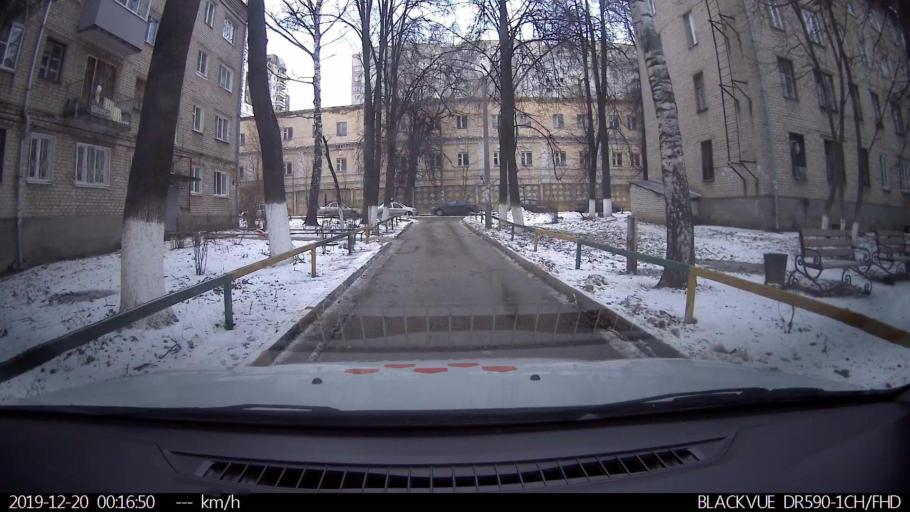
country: RU
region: Jaroslavl
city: Petrovsk
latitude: 56.9405
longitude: 39.4079
